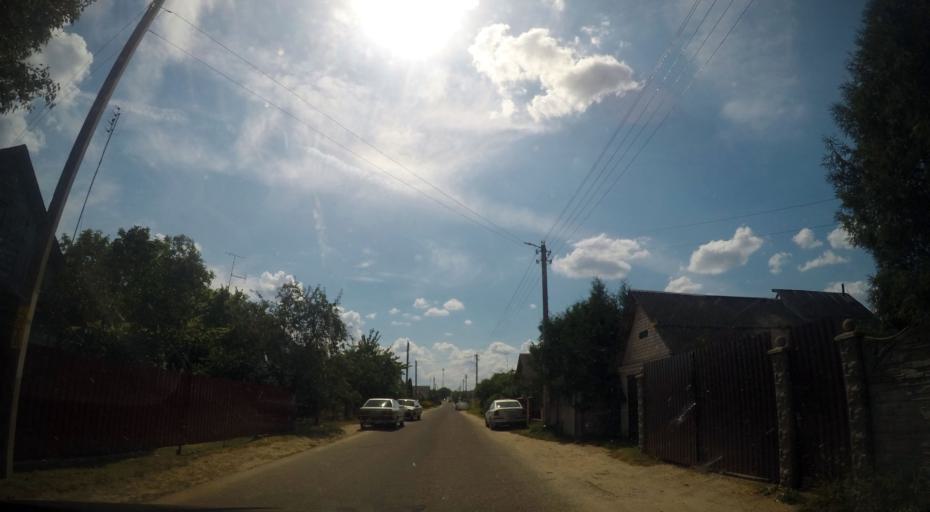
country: BY
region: Grodnenskaya
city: Hrodna
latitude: 53.6262
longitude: 23.8393
